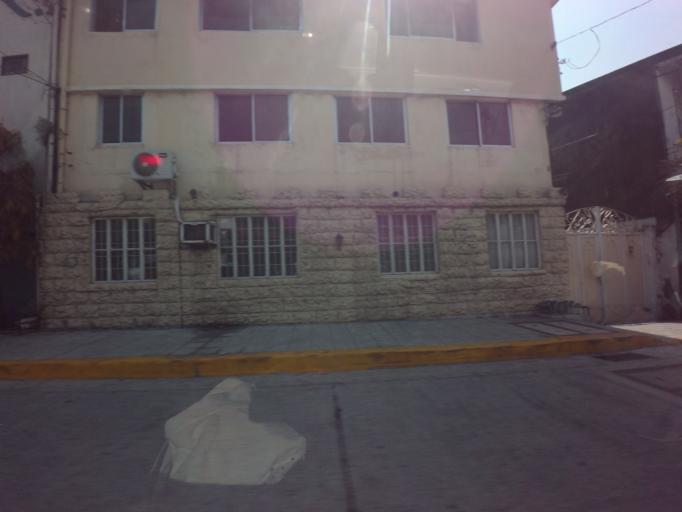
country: PH
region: Metro Manila
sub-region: Makati City
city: Makati City
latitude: 14.5639
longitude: 121.0050
